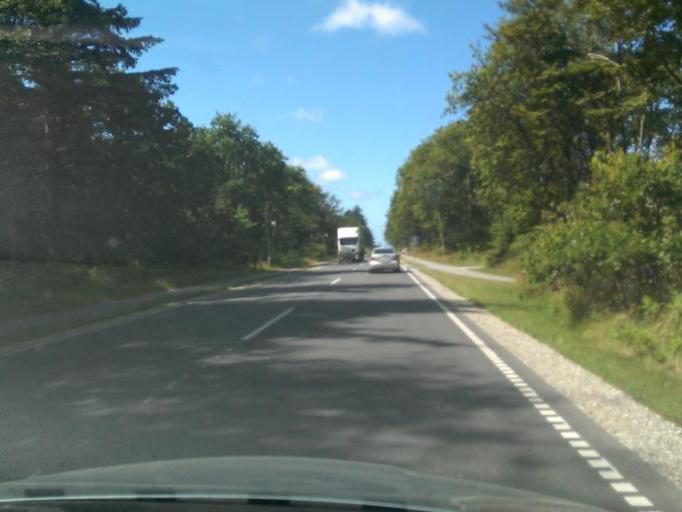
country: DK
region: North Denmark
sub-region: Jammerbugt Kommune
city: Pandrup
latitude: 57.2494
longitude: 9.6078
